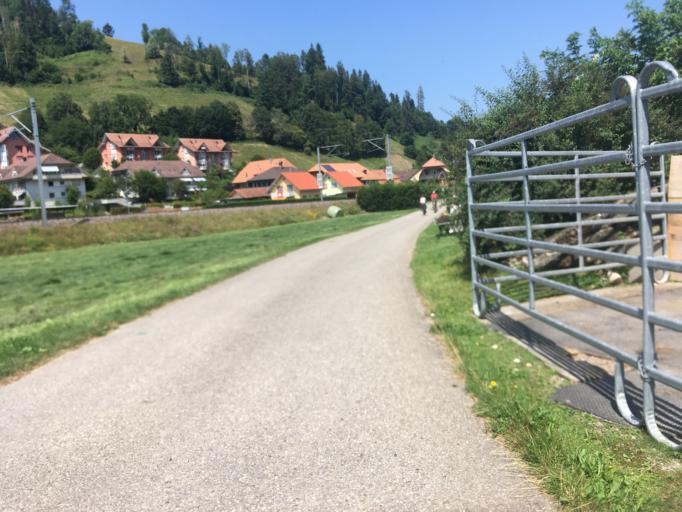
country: CH
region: Bern
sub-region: Emmental District
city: Signau
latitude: 46.9153
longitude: 7.7207
